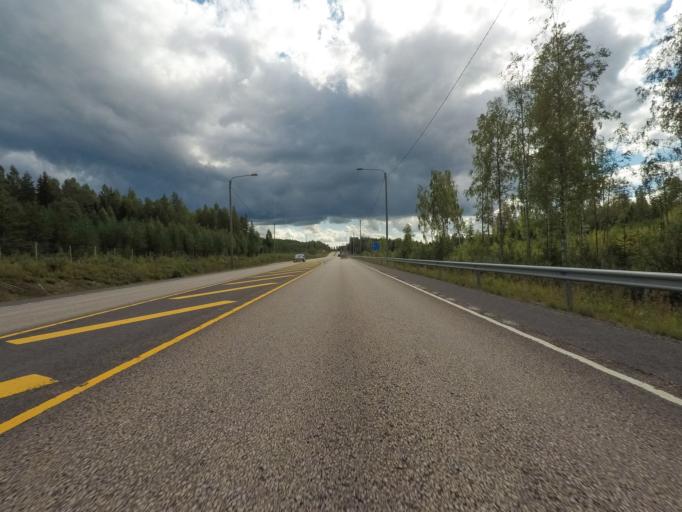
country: FI
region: Central Finland
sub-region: Joutsa
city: Leivonmaeki
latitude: 61.9920
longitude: 26.0584
